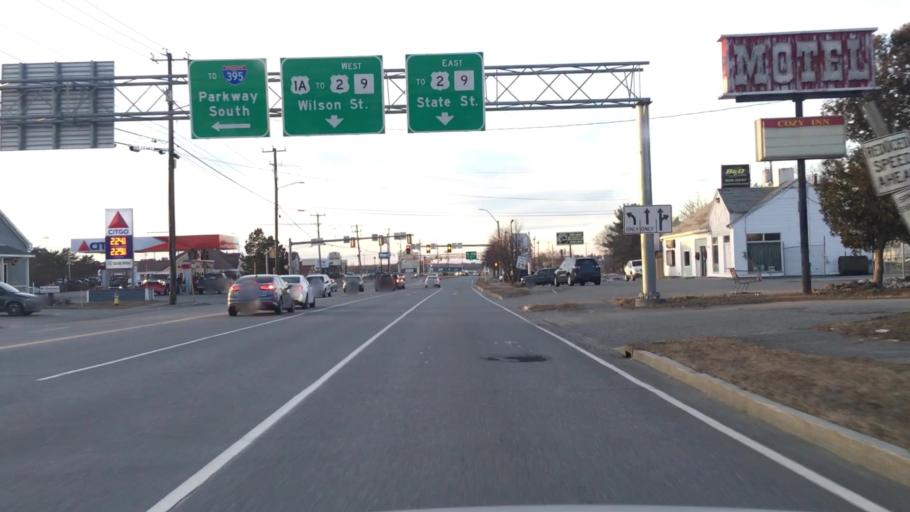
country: US
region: Maine
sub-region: Penobscot County
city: Brewer
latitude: 44.7831
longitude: -68.7490
